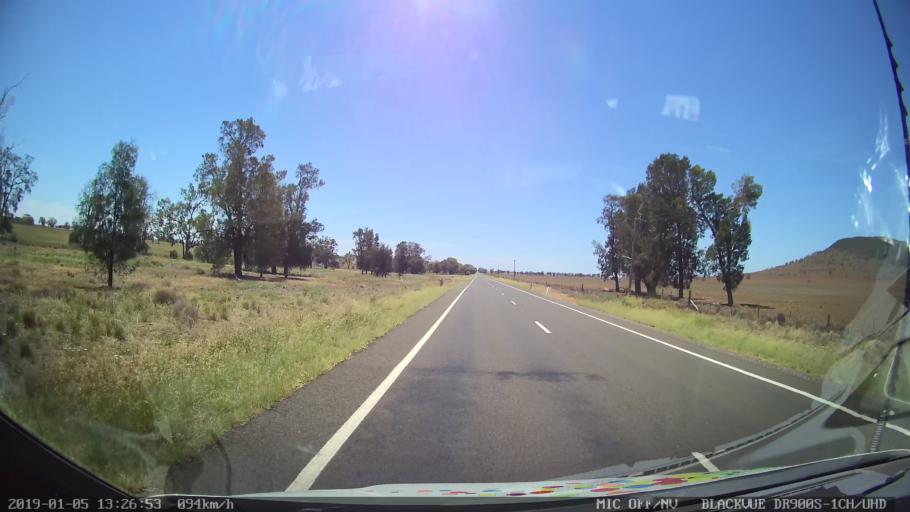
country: AU
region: New South Wales
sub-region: Gunnedah
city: Gunnedah
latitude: -31.0492
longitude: 150.0218
